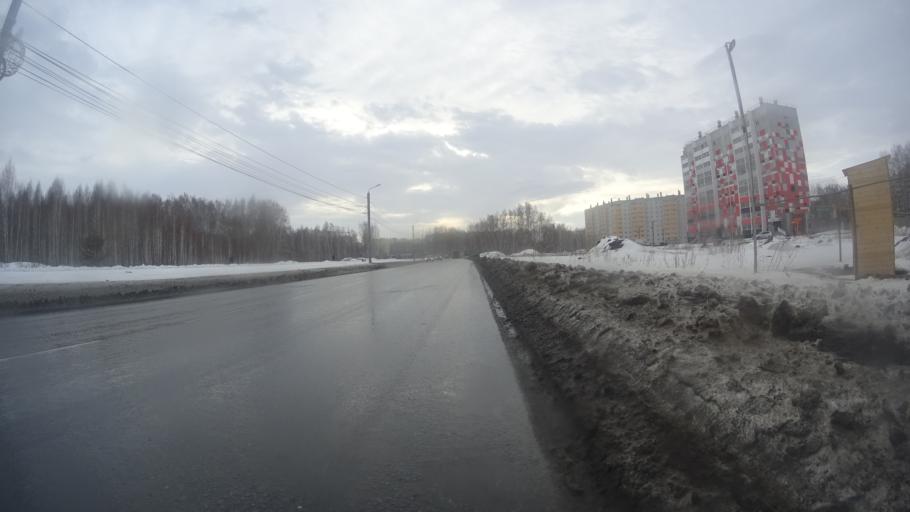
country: RU
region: Chelyabinsk
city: Roshchino
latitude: 55.2170
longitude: 61.2891
